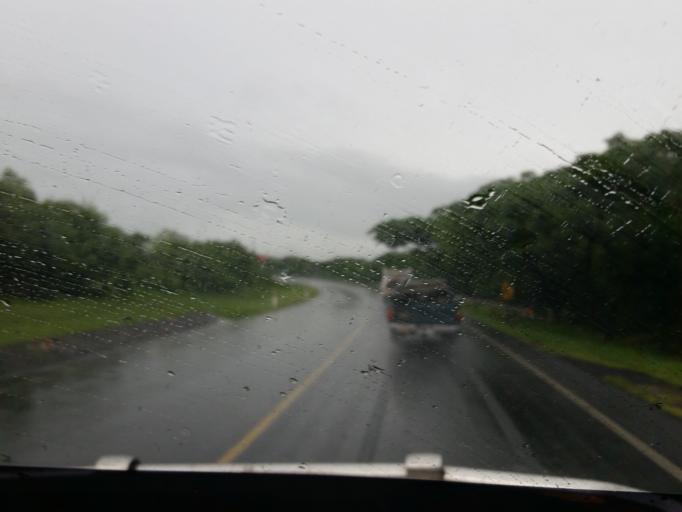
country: NI
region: Matagalpa
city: Ciudad Dario
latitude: 12.7340
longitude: -86.1148
